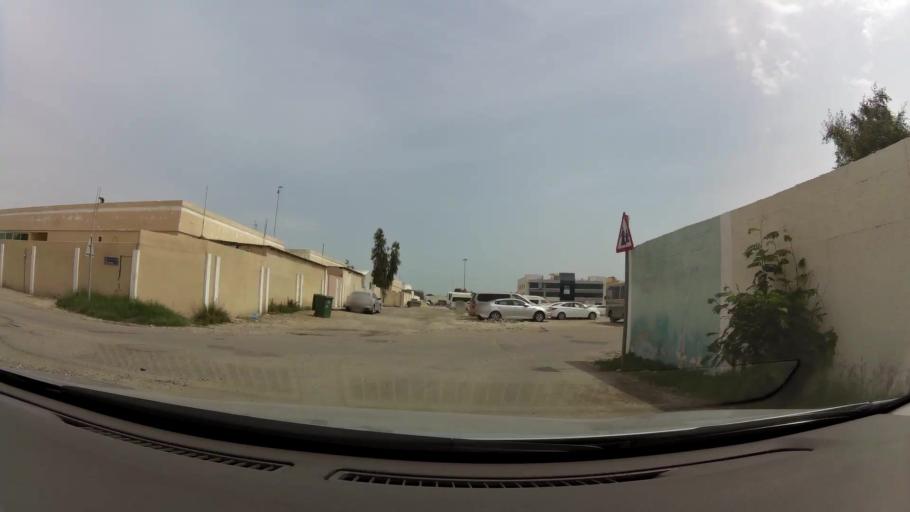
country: QA
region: Baladiyat ad Dawhah
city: Doha
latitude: 25.2645
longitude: 51.4948
